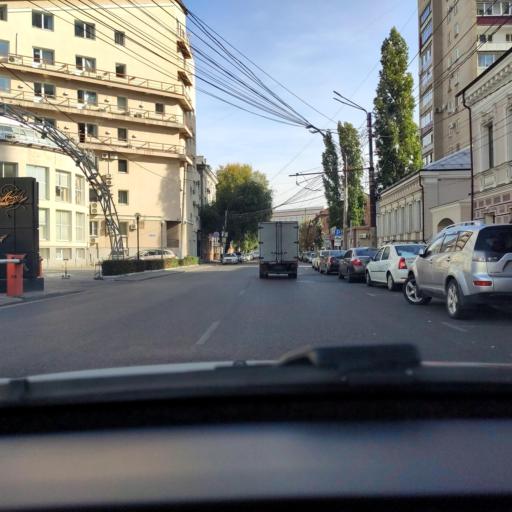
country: RU
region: Voronezj
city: Voronezh
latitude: 51.6579
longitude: 39.2022
